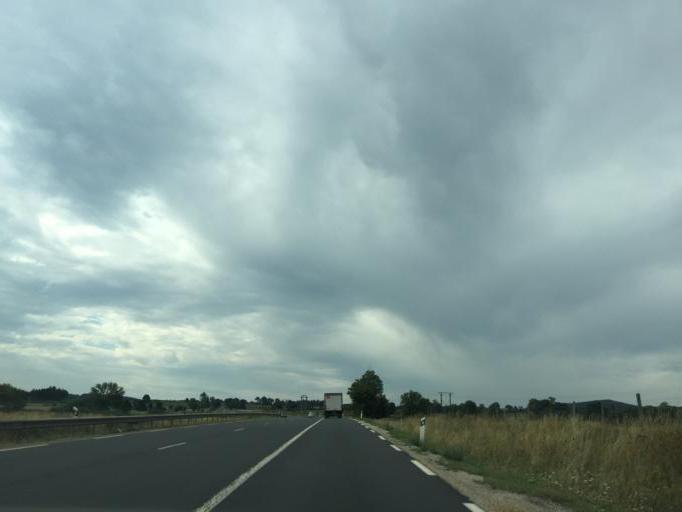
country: FR
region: Auvergne
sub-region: Departement de la Haute-Loire
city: Solignac-sur-Loire
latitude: 44.9221
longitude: 3.8438
